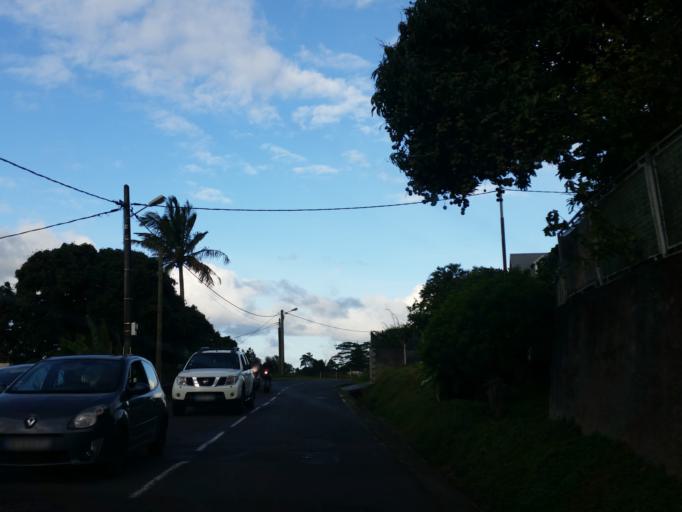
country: RE
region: Reunion
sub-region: Reunion
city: Saint-Denis
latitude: -20.8854
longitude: 55.4237
